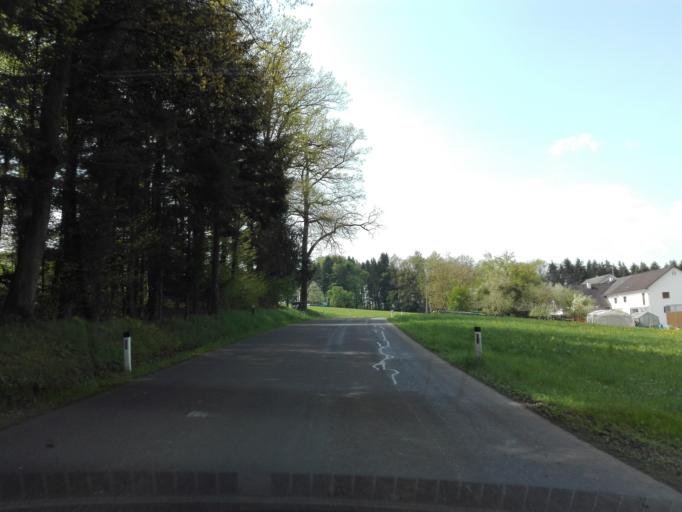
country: AT
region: Upper Austria
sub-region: Politischer Bezirk Perg
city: Perg
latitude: 48.2480
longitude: 14.7055
